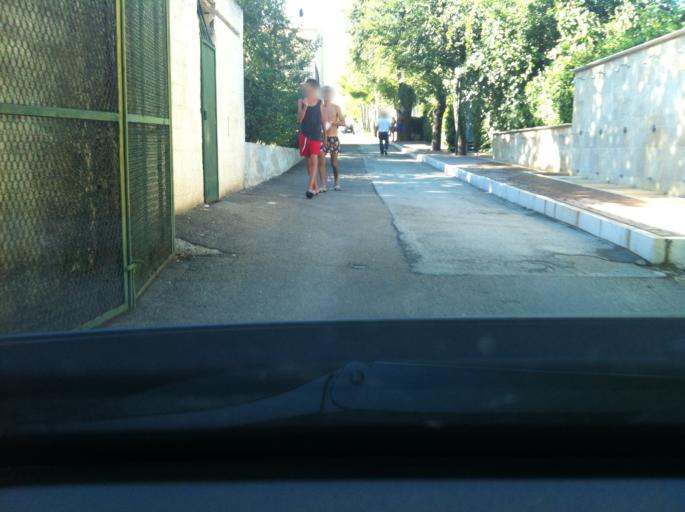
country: IT
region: Apulia
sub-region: Provincia di Foggia
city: Monte Sant'Angelo
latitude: 41.6562
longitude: 15.9772
